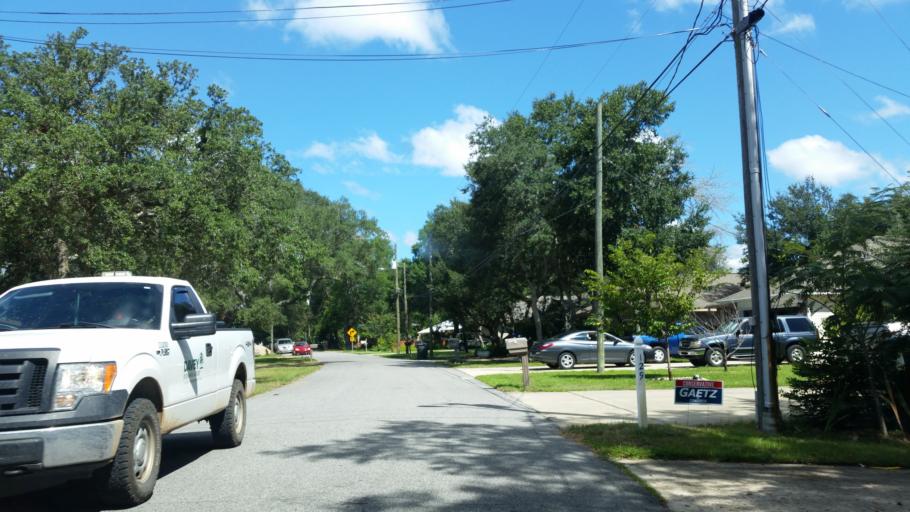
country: US
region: Florida
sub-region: Okaloosa County
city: Fort Walton Beach
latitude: 30.4217
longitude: -86.6150
